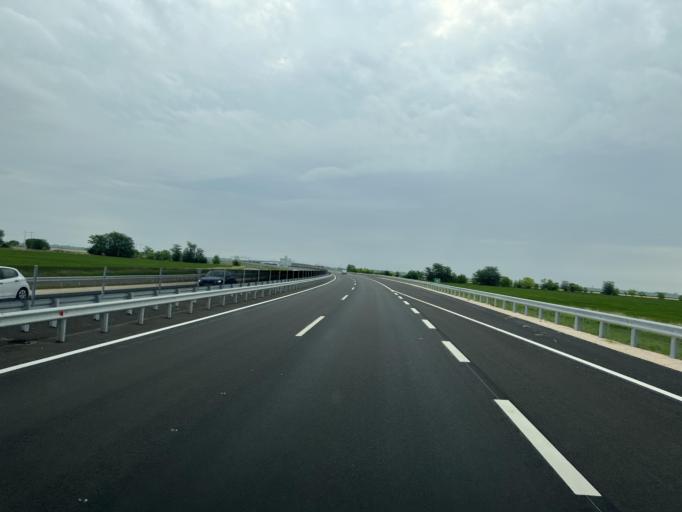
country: HU
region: Pest
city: Abony
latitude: 47.2058
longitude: 20.0805
